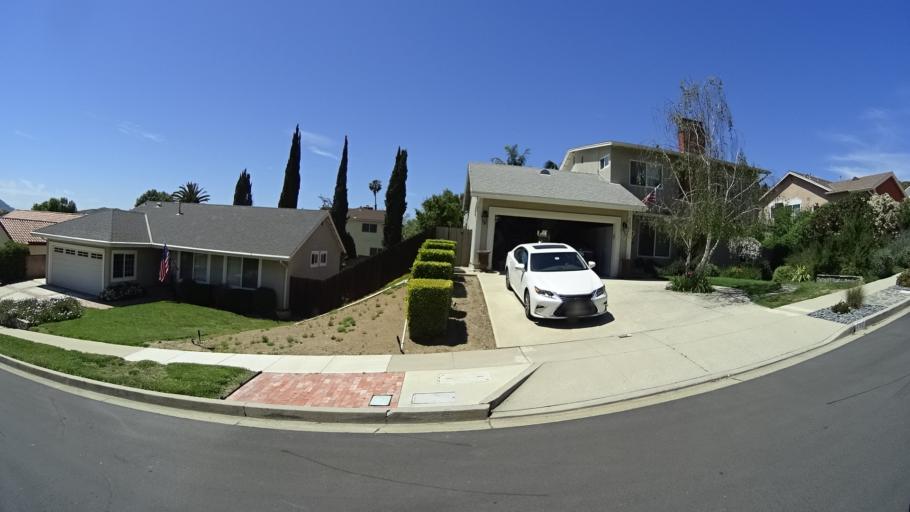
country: US
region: California
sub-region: Ventura County
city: Casa Conejo
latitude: 34.1650
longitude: -118.9475
